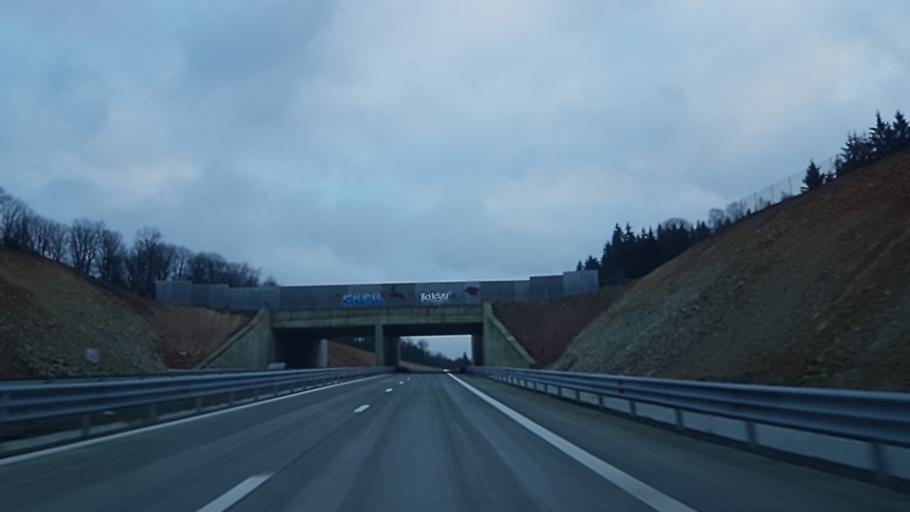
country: BE
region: Wallonia
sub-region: Province de Namur
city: Couvin
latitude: 50.0025
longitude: 4.5404
